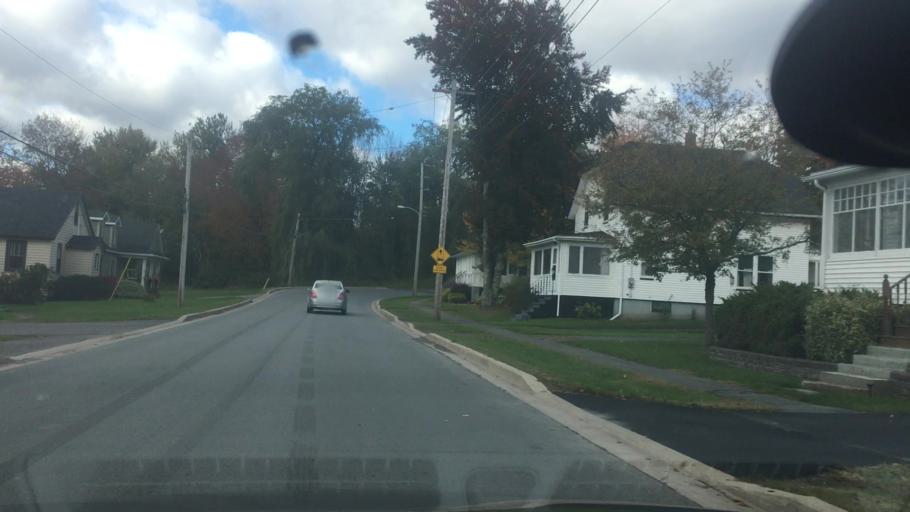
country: CA
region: Nova Scotia
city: Windsor
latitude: 44.9856
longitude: -64.1322
